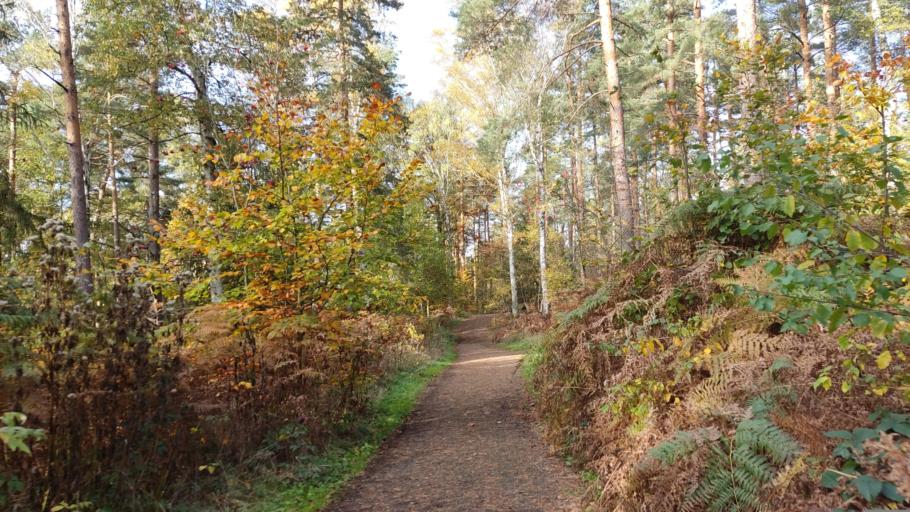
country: DE
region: Saxony
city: Struppen
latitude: 50.8974
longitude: 14.0328
